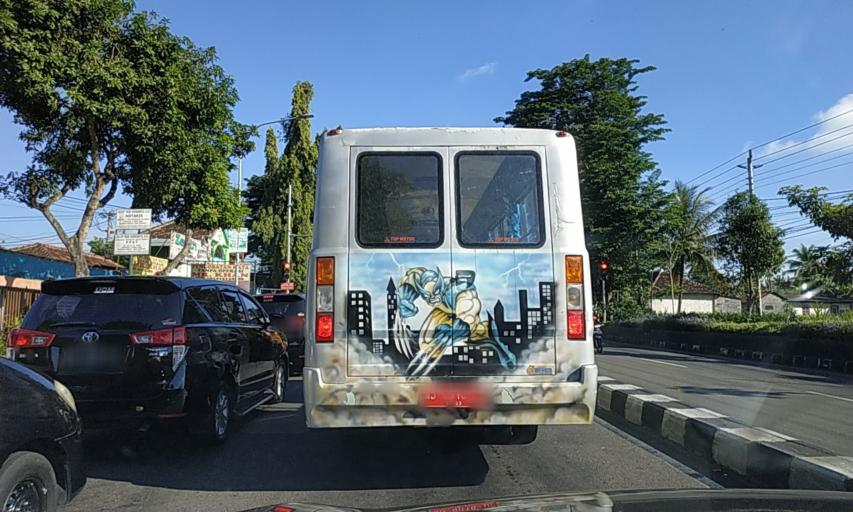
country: ID
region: Daerah Istimewa Yogyakarta
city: Sleman
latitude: -7.7119
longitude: 110.3579
